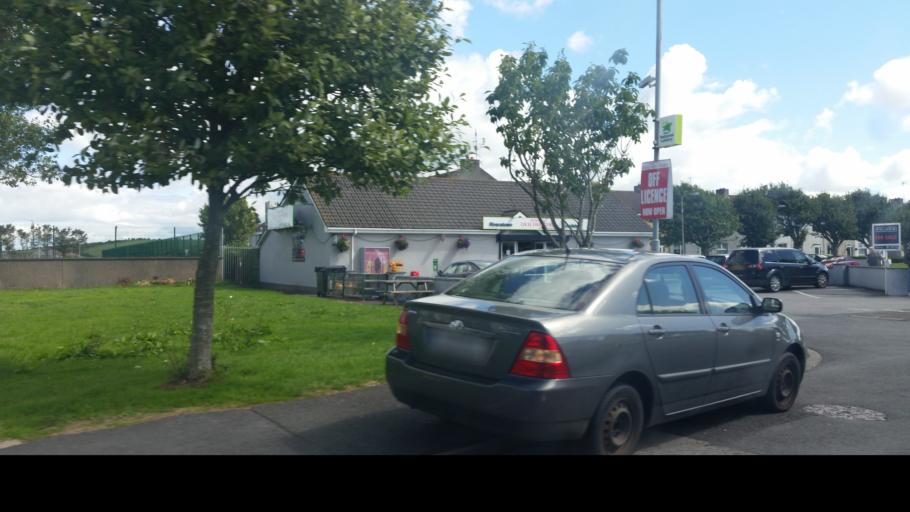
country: IE
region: Munster
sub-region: Waterford
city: Tra Mhor
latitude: 52.1676
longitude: -7.1416
